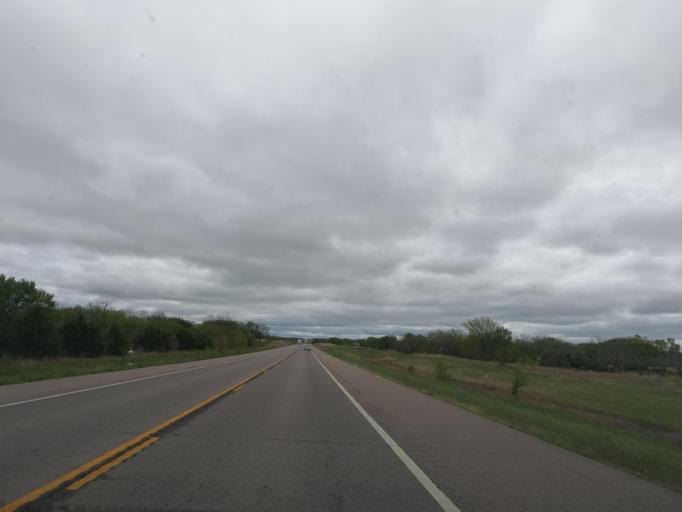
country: US
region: Kansas
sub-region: Elk County
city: Howard
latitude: 37.6364
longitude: -96.3738
